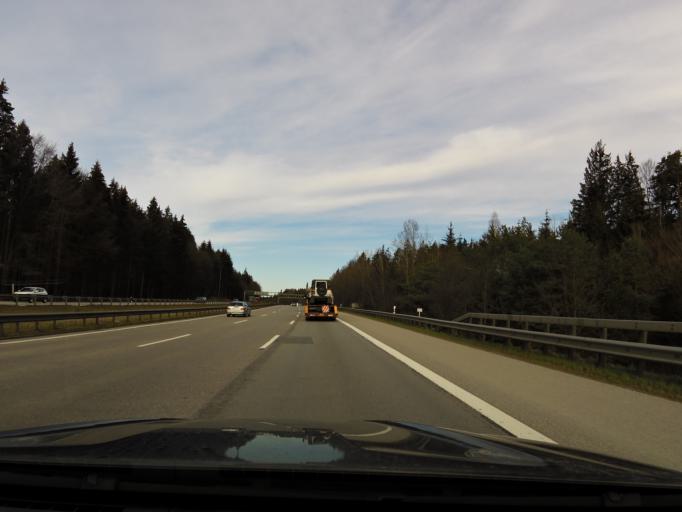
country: DE
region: Bavaria
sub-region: Upper Bavaria
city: Weyarn
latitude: 47.8647
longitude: 11.8295
